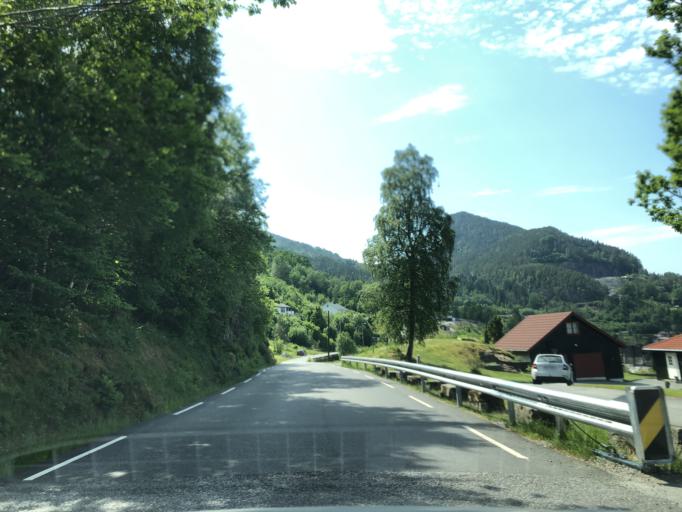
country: NO
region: Hordaland
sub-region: Jondal
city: Jondal
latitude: 60.3063
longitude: 6.2950
